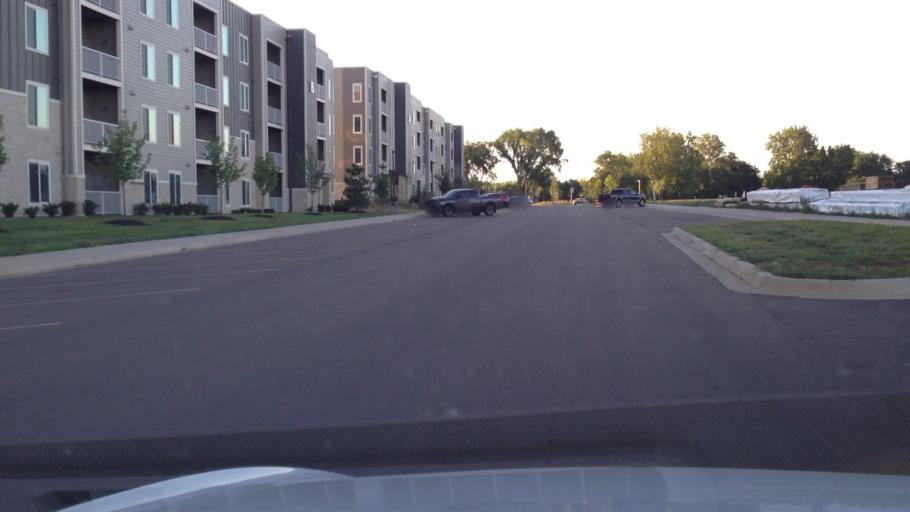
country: US
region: Kansas
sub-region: Douglas County
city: Lawrence
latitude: 38.9527
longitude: -95.2918
